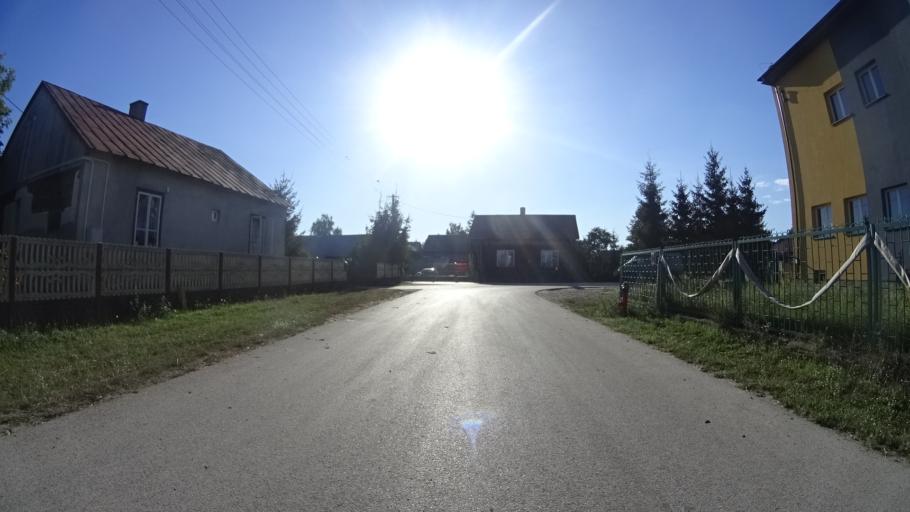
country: PL
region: Masovian Voivodeship
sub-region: Powiat bialobrzeski
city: Wysmierzyce
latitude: 51.6514
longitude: 20.7849
